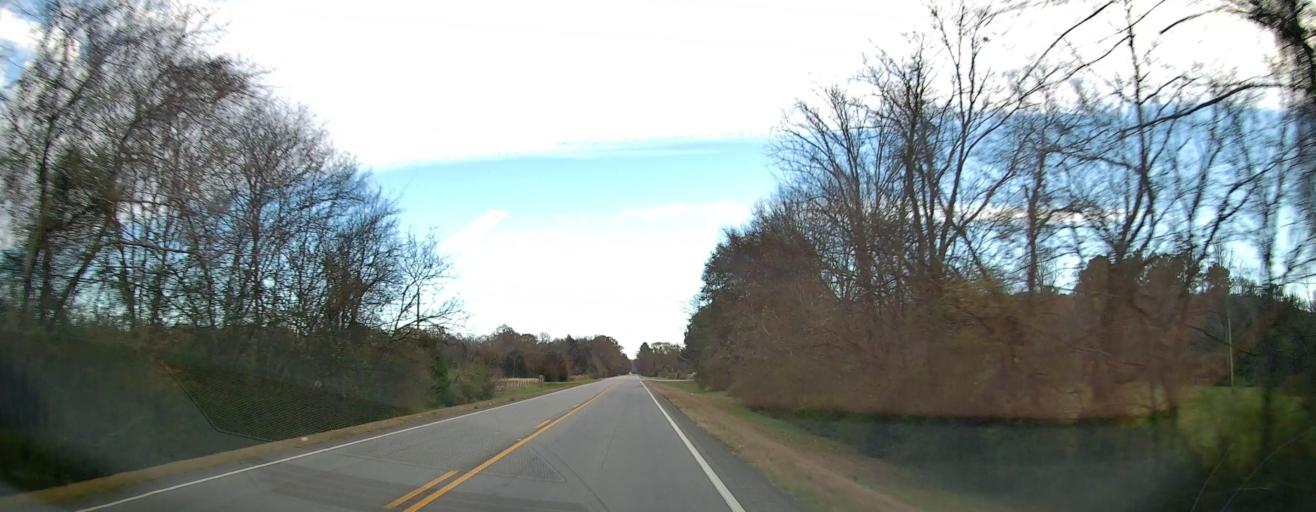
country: US
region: Alabama
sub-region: Marshall County
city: Arab
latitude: 34.3970
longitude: -86.6784
